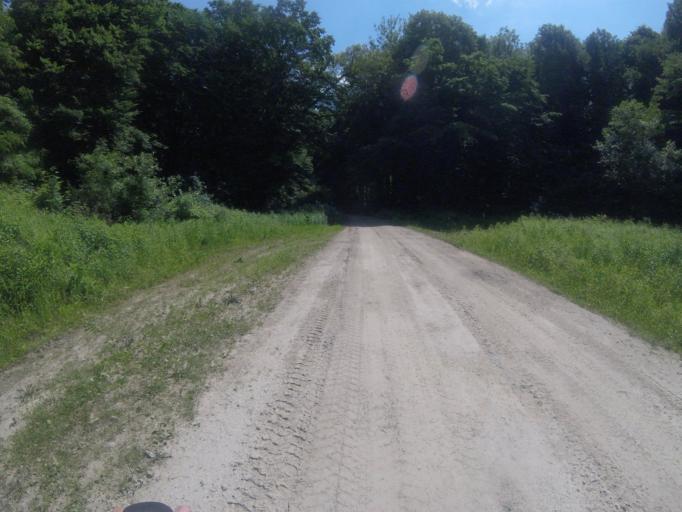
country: HU
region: Veszprem
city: Cseteny
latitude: 47.2647
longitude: 17.9990
